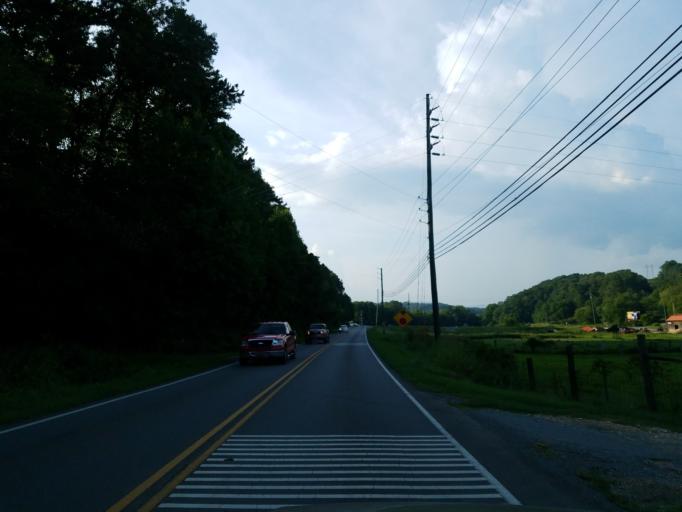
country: US
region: Georgia
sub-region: Gilmer County
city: Ellijay
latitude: 34.6583
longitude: -84.5000
